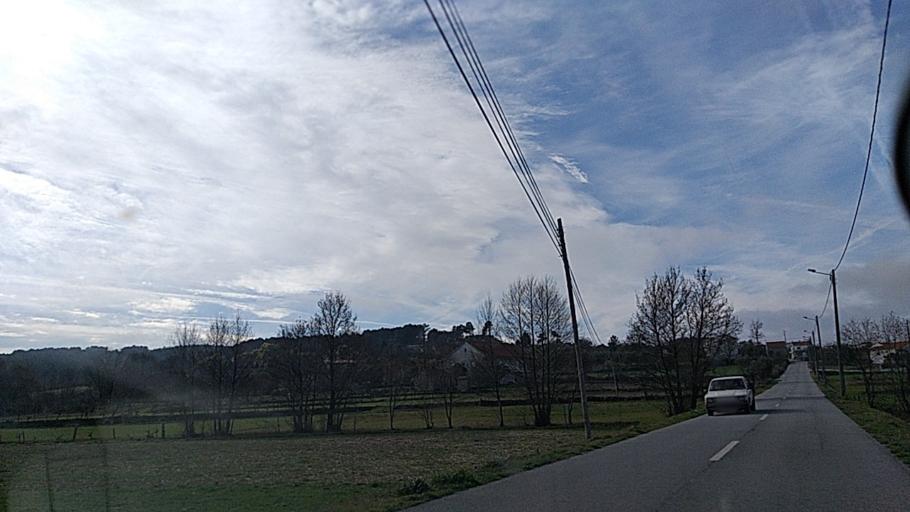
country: PT
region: Guarda
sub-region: Fornos de Algodres
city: Fornos de Algodres
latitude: 40.6604
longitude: -7.5321
